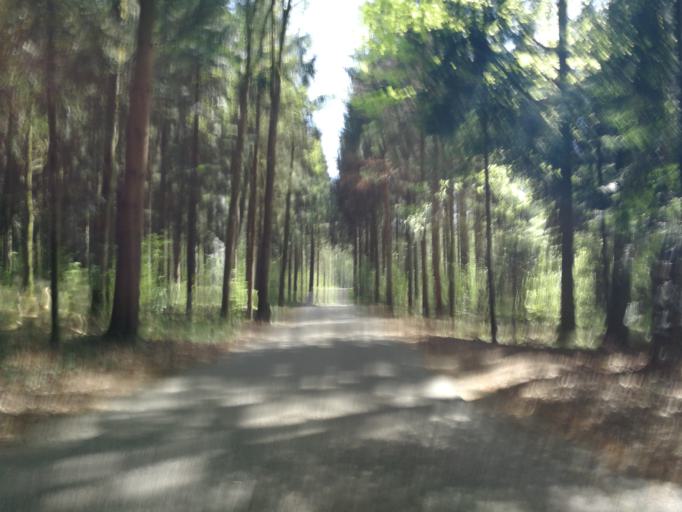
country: CH
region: Zurich
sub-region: Bezirk Hinwil
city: Hinwil
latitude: 47.2981
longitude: 8.8210
